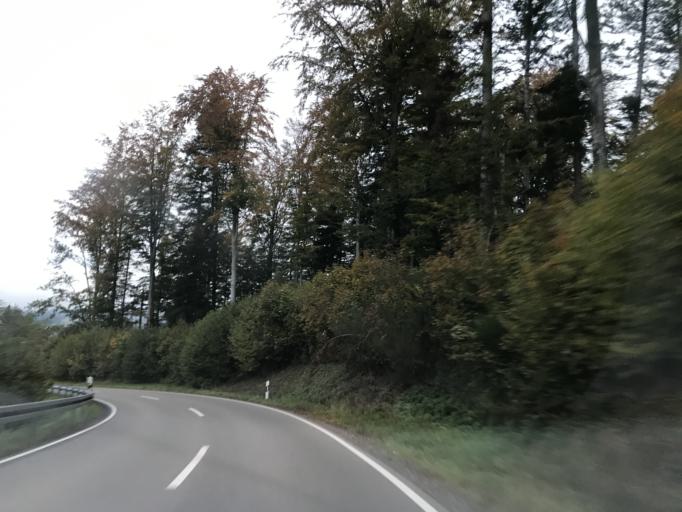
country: DE
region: Baden-Wuerttemberg
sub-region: Freiburg Region
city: Rickenbach
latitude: 47.6213
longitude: 8.0252
